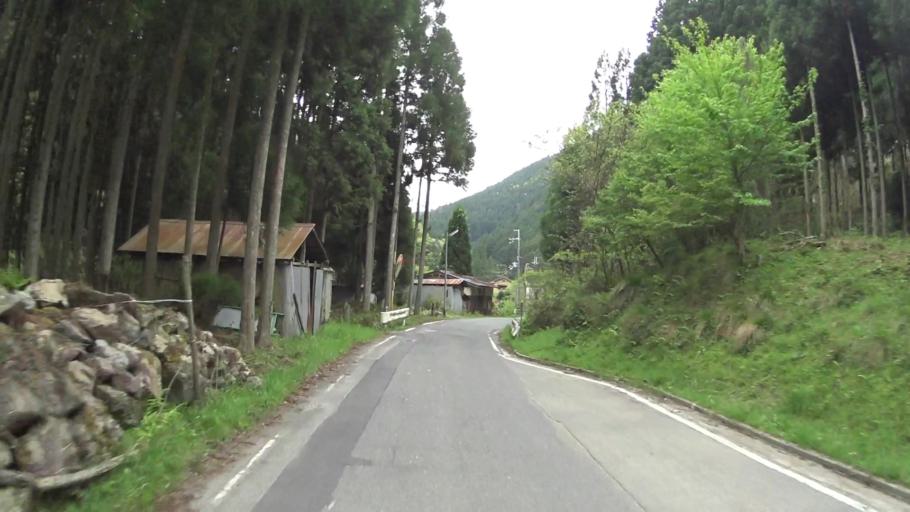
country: JP
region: Kyoto
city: Kameoka
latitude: 35.1234
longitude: 135.6227
